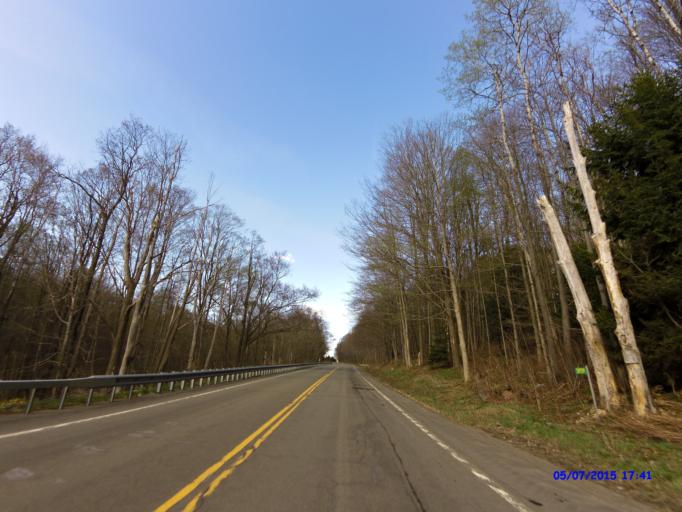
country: US
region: New York
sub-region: Cattaraugus County
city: Franklinville
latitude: 42.2934
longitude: -78.5248
